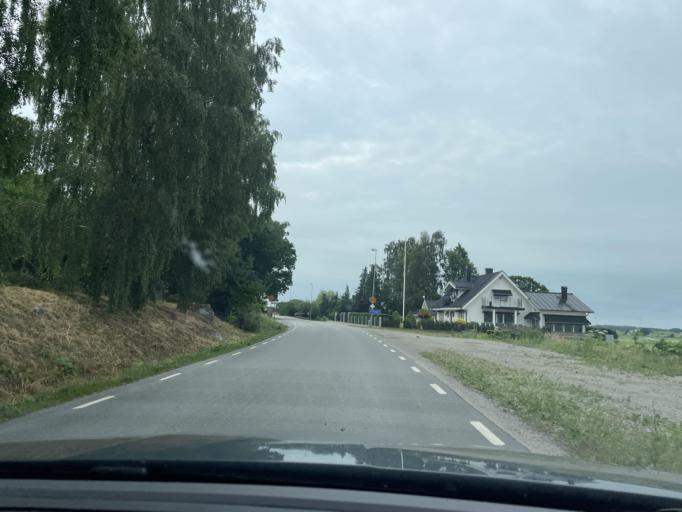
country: SE
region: Blekinge
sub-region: Solvesborgs Kommun
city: Soelvesborg
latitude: 56.0340
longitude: 14.6363
